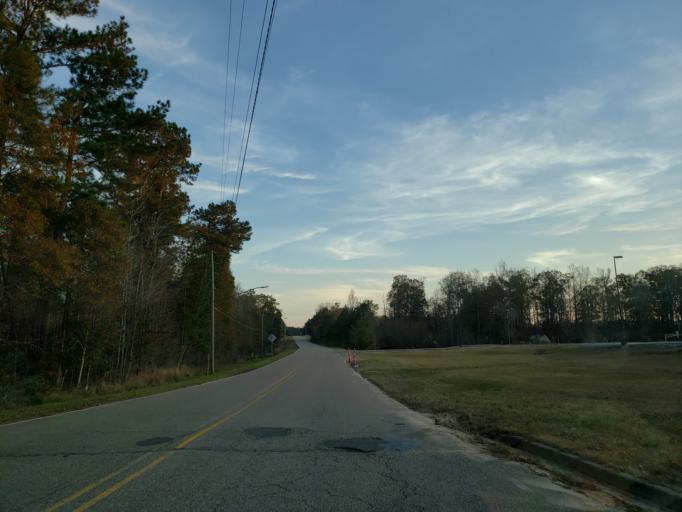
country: US
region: Mississippi
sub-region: Forrest County
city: Hattiesburg
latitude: 31.2894
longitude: -89.3130
